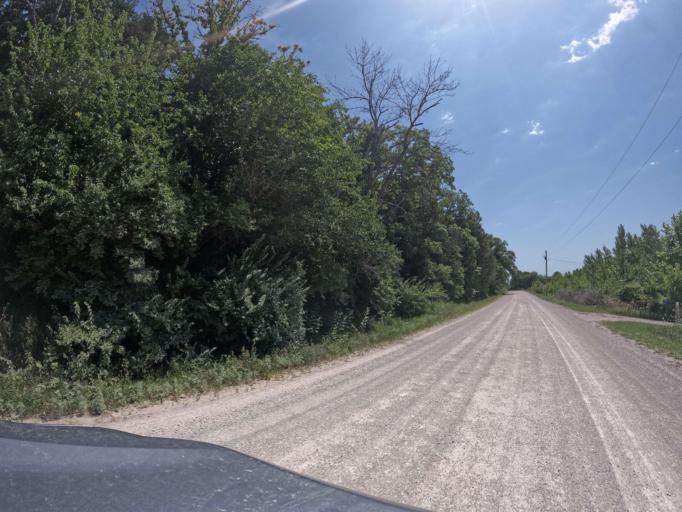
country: US
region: Iowa
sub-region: Henry County
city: Mount Pleasant
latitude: 40.8961
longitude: -91.5494
